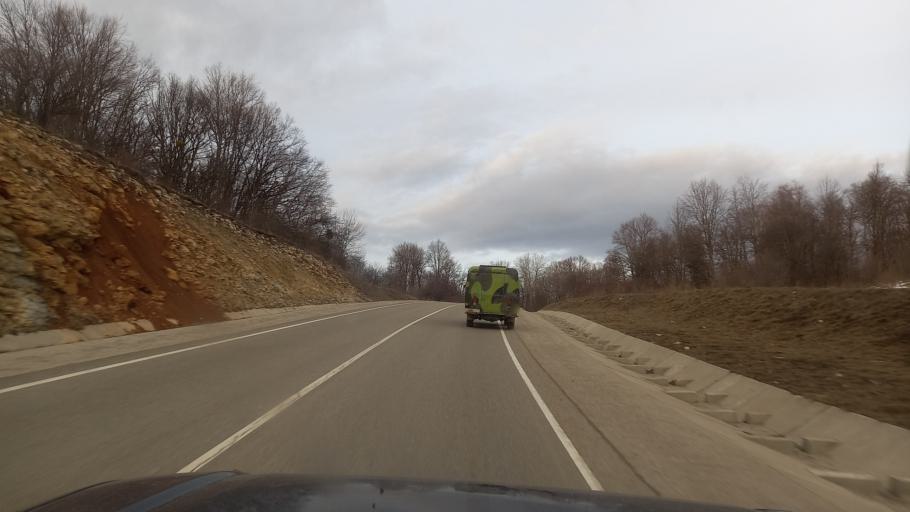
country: RU
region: Adygeya
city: Kamennomostskiy
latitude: 44.2206
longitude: 39.9792
